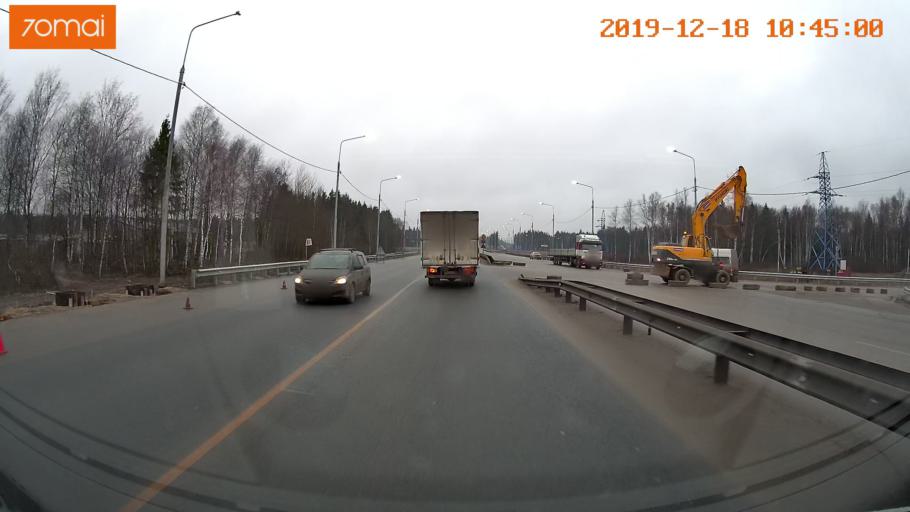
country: RU
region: Moskovskaya
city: Aprelevka
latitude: 55.4757
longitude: 37.0658
